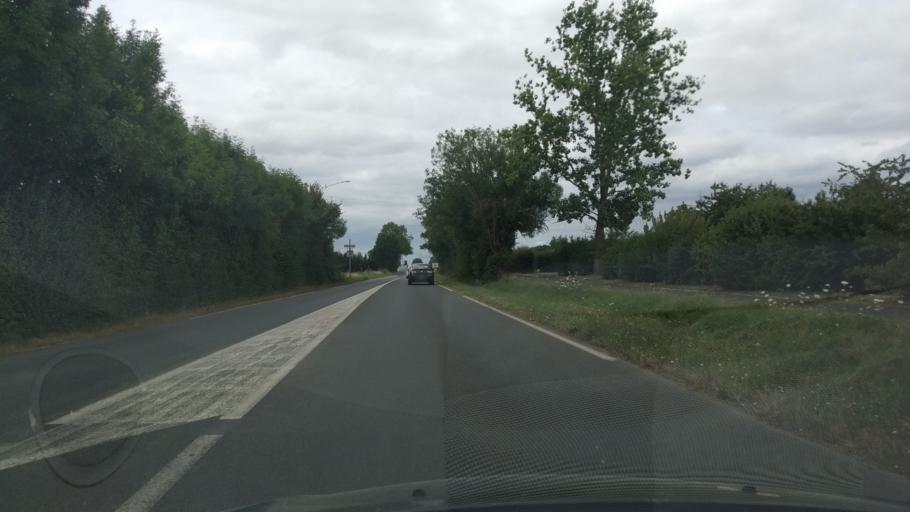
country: FR
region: Poitou-Charentes
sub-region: Departement de la Vienne
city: Roches-Premarie-Andille
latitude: 46.4907
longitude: 0.3677
